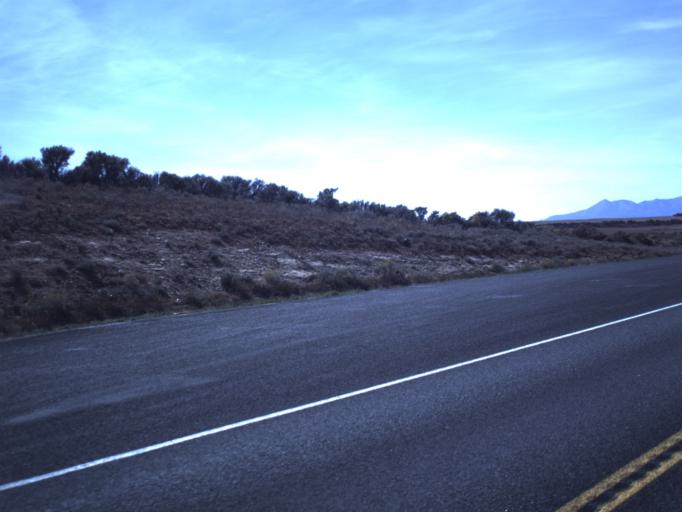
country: US
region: Colorado
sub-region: Dolores County
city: Dove Creek
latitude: 37.8171
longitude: -109.0442
